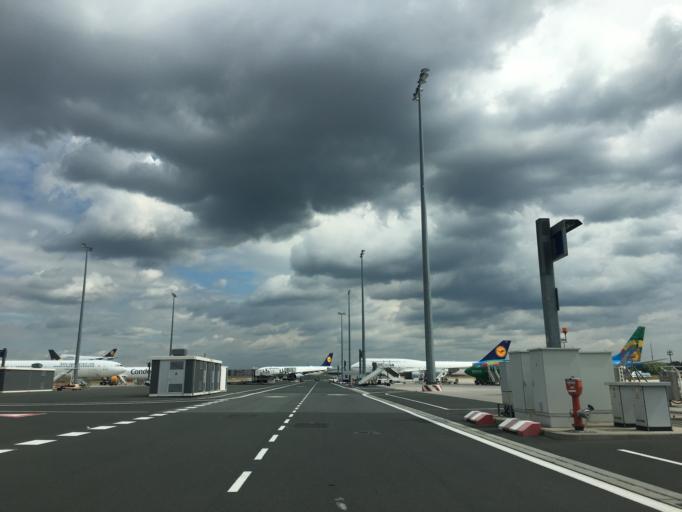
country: DE
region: Hesse
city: Morfelden-Walldorf
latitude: 50.0334
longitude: 8.5858
